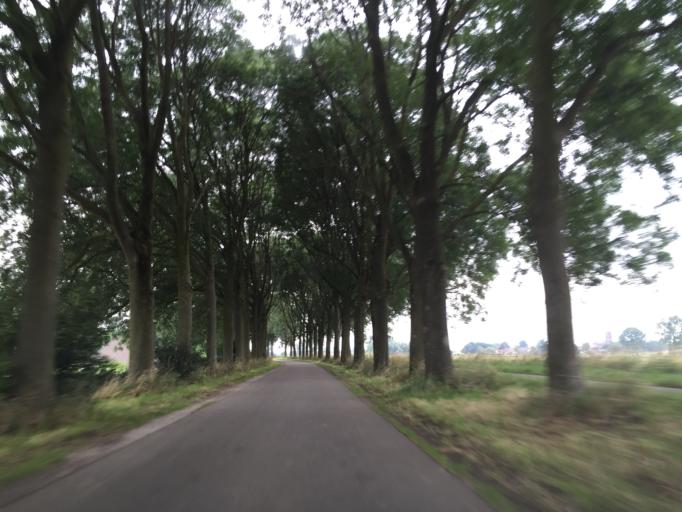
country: NL
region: Gelderland
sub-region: Gemeente Wijchen
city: Bergharen
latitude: 51.8149
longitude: 5.6378
